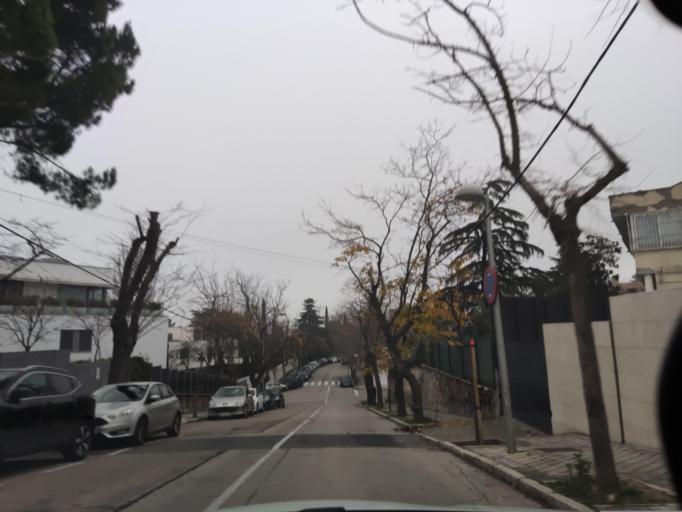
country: ES
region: Madrid
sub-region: Provincia de Madrid
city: Tetuan de las Victorias
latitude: 40.4864
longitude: -3.7105
